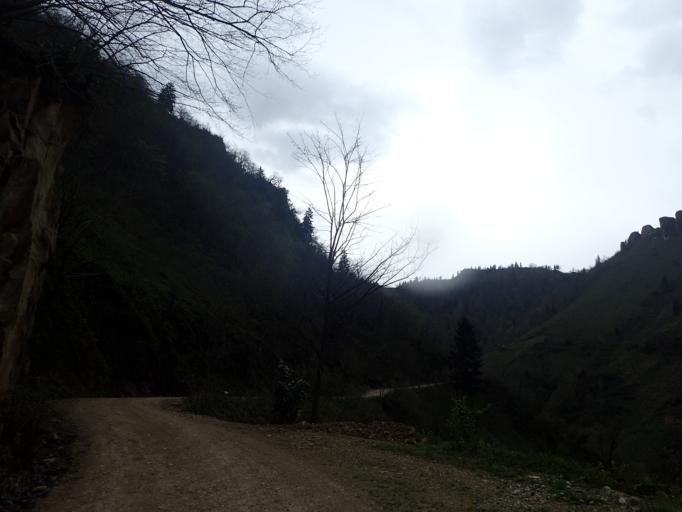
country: TR
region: Ordu
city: Kabaduz
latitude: 40.7861
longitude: 37.8883
